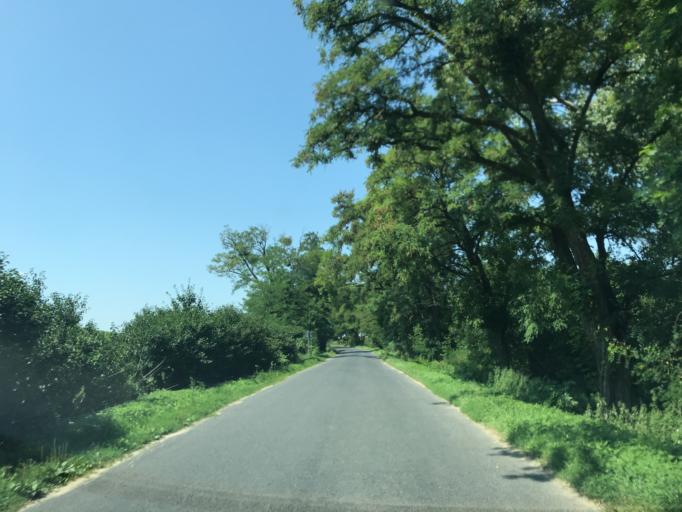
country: PL
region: Kujawsko-Pomorskie
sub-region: Powiat lipnowski
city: Chrostkowo
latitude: 52.9936
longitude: 19.2389
